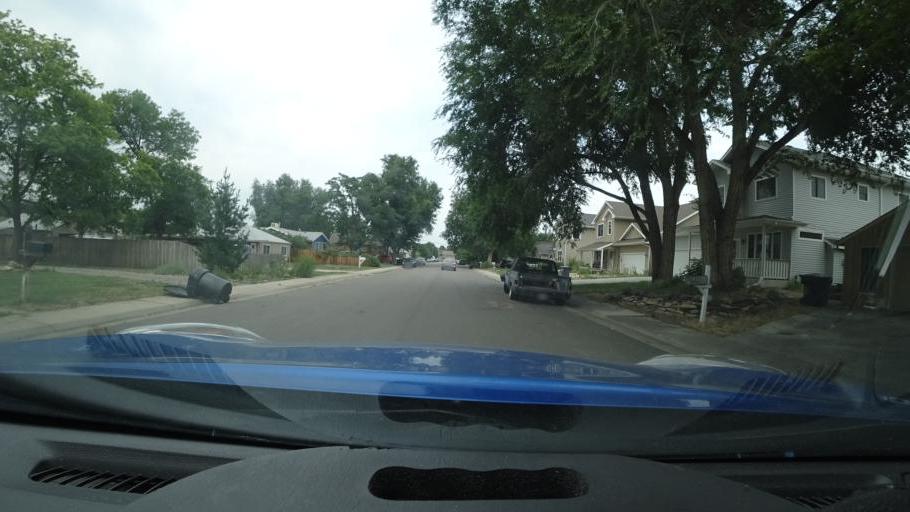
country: US
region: Colorado
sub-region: Arapahoe County
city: Glendale
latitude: 39.7010
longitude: -104.9164
